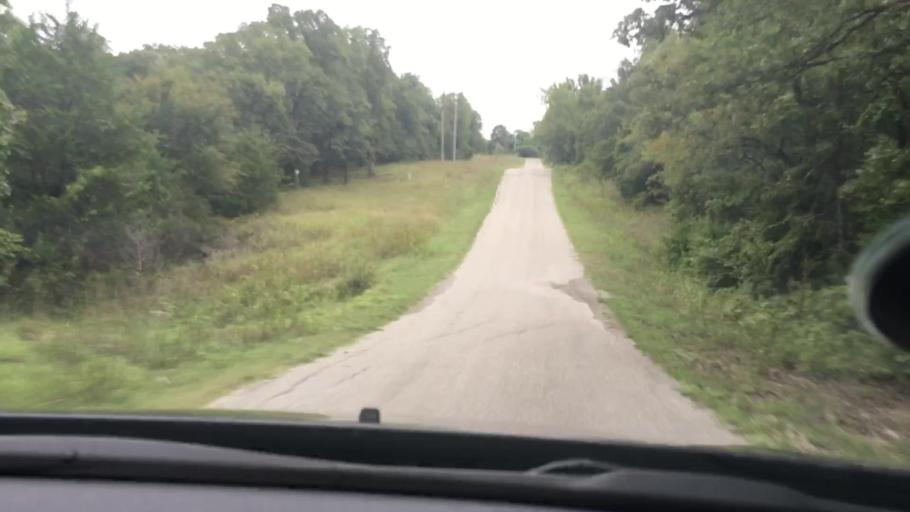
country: US
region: Oklahoma
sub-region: Pontotoc County
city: Byng
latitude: 34.8150
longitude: -96.5474
